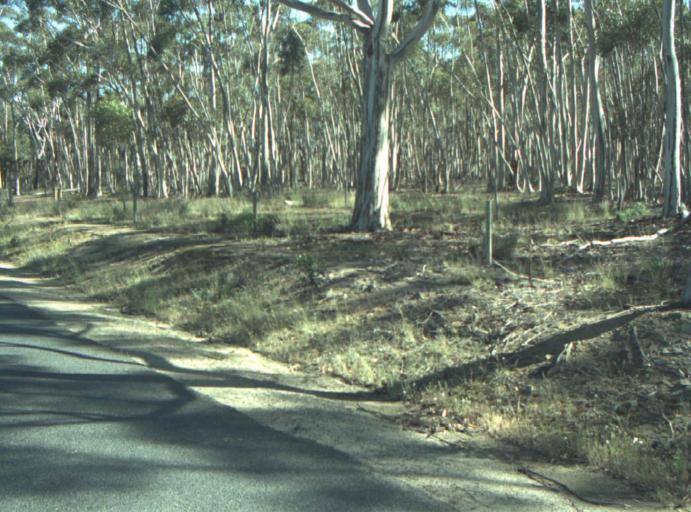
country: AU
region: Victoria
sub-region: Greater Geelong
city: Lara
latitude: -37.9645
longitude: 144.4058
